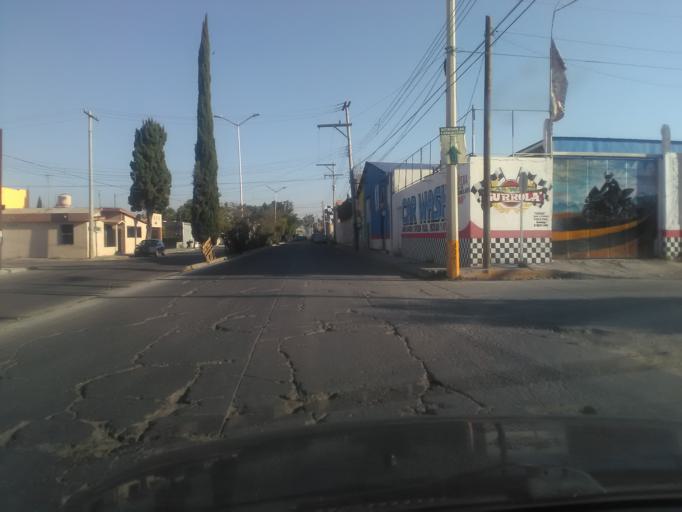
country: MX
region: Durango
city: Victoria de Durango
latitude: 24.0412
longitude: -104.6207
